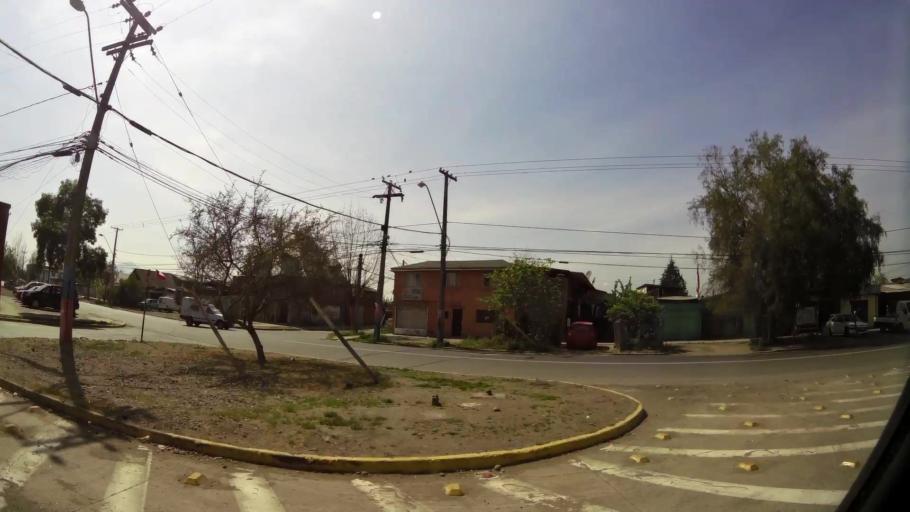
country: CL
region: Santiago Metropolitan
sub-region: Provincia de Santiago
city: Lo Prado
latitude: -33.4312
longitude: -70.7504
